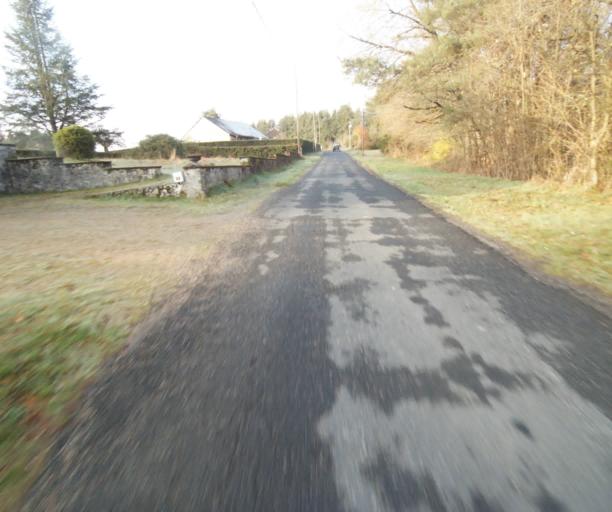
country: FR
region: Limousin
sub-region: Departement de la Correze
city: Correze
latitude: 45.3253
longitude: 1.8663
